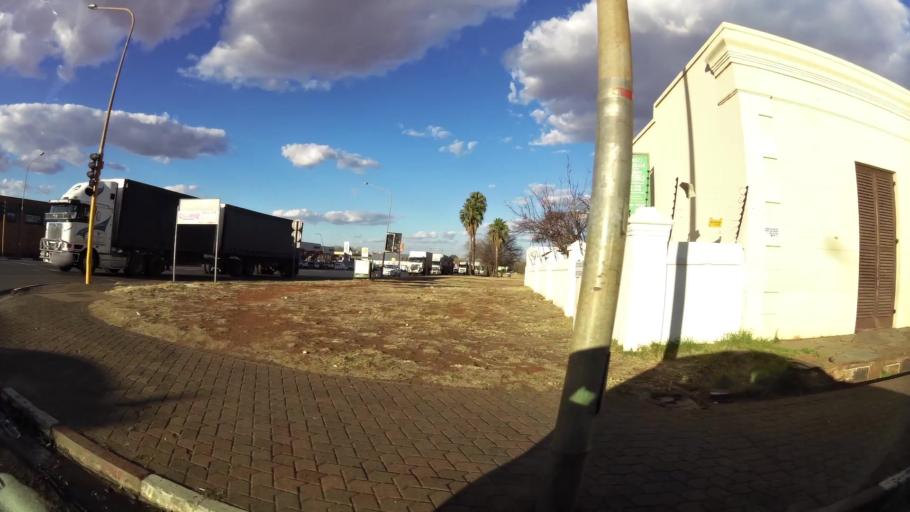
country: ZA
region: North-West
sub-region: Dr Kenneth Kaunda District Municipality
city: Potchefstroom
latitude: -26.7150
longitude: 27.0990
